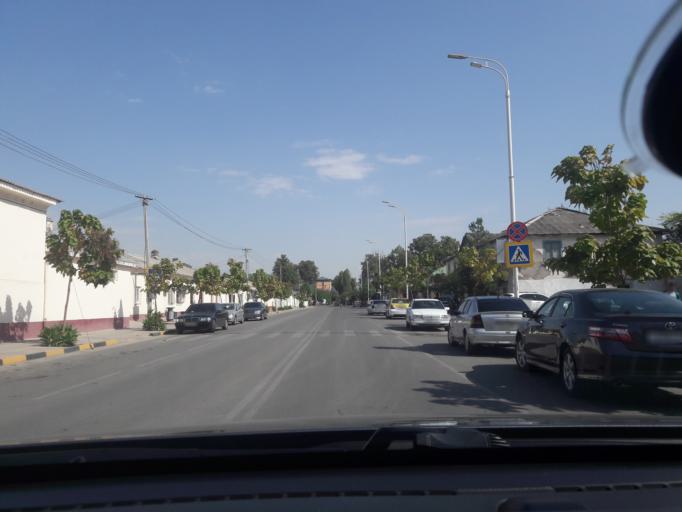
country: TJ
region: Dushanbe
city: Dushanbe
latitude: 38.5655
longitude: 68.8024
